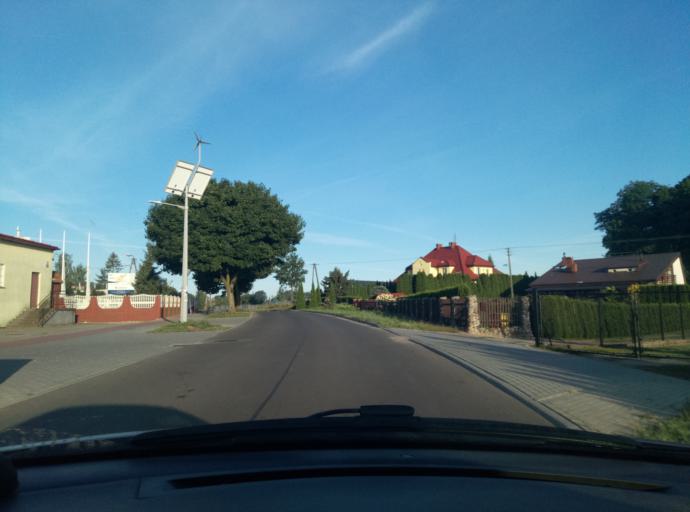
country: PL
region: Kujawsko-Pomorskie
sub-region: Powiat brodnicki
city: Jablonowo Pomorskie
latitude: 53.3900
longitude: 19.1468
